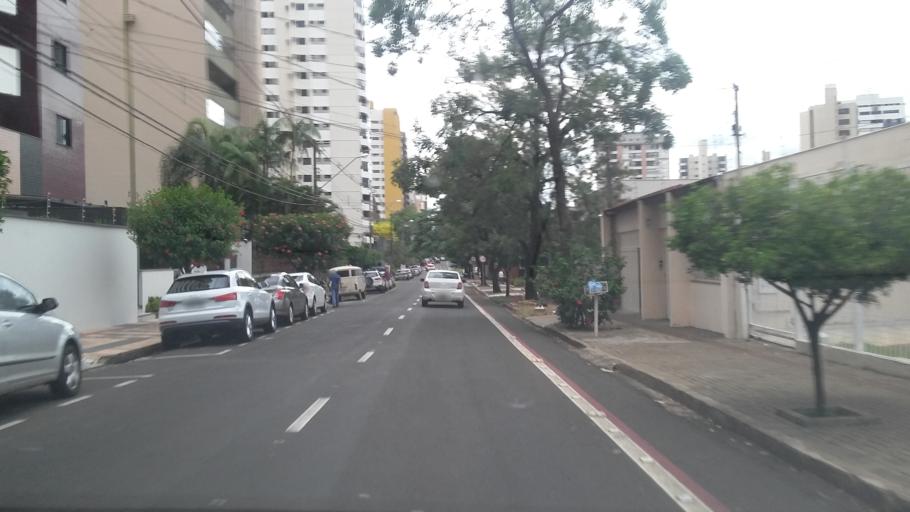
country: BR
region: Parana
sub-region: Londrina
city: Londrina
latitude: -23.3177
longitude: -51.1676
